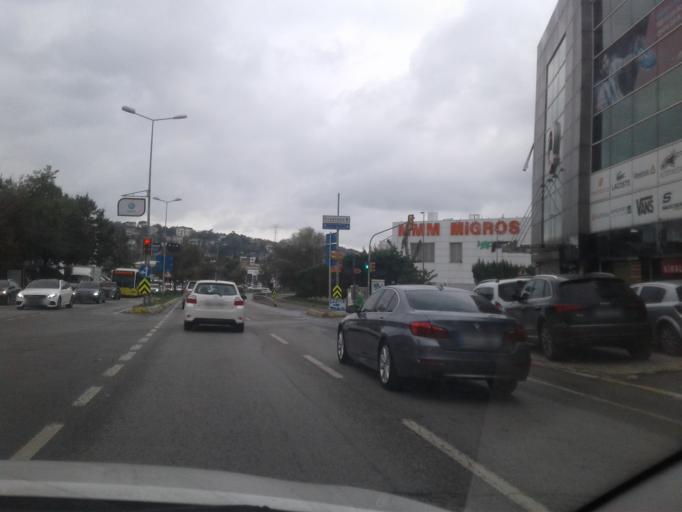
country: TR
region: Istanbul
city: Umraniye
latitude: 41.0813
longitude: 29.0805
